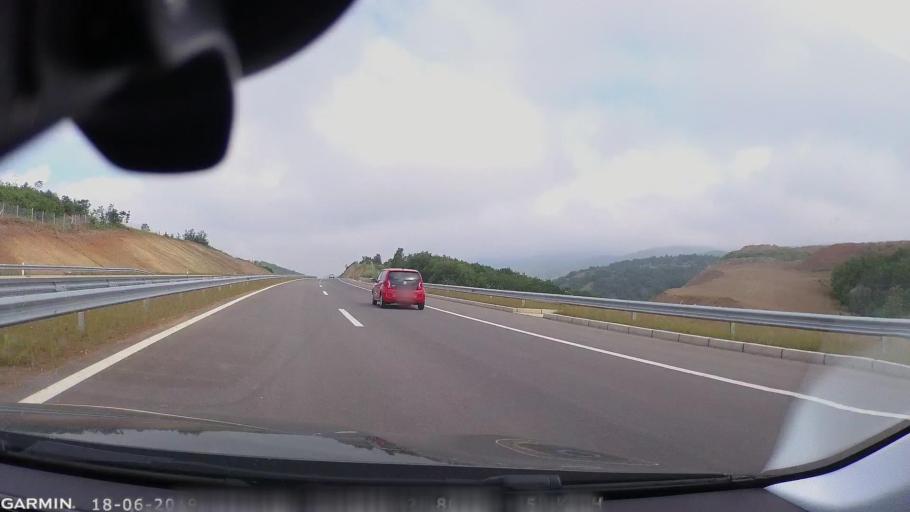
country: MK
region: Sveti Nikole
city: Gorobinci
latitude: 41.9203
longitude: 21.8669
